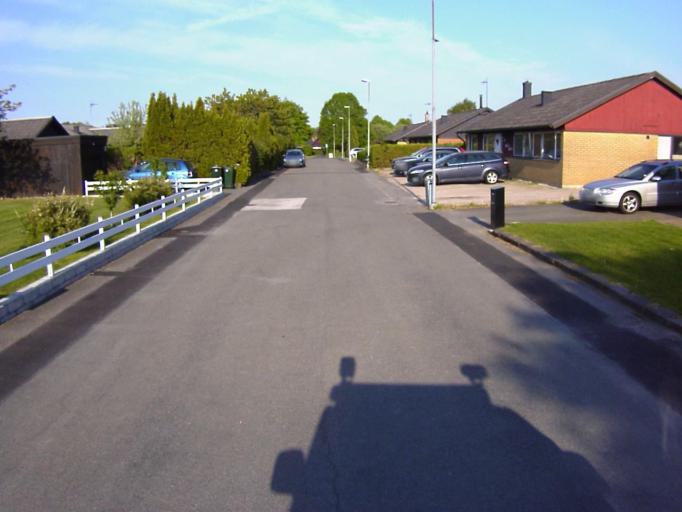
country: SE
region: Skane
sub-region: Kristianstads Kommun
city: Onnestad
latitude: 56.0551
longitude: 14.0184
